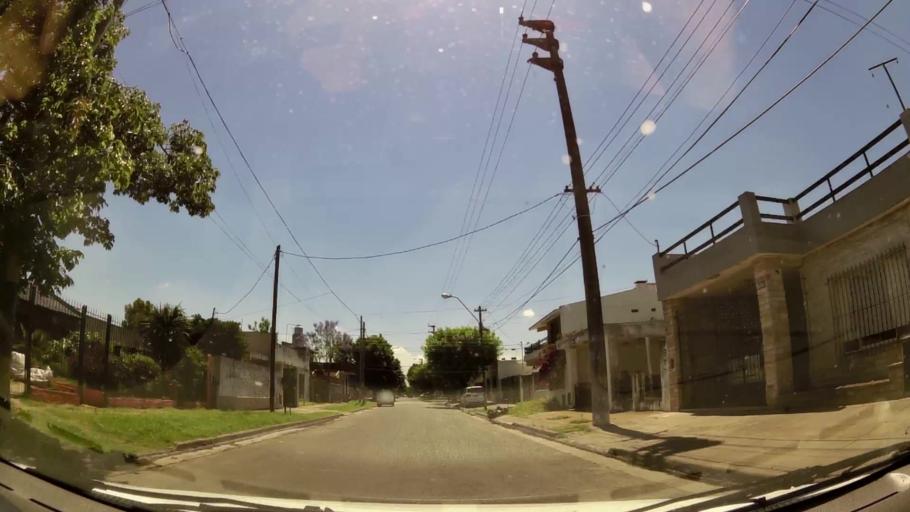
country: AR
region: Buenos Aires
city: Ituzaingo
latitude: -34.6602
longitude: -58.6801
